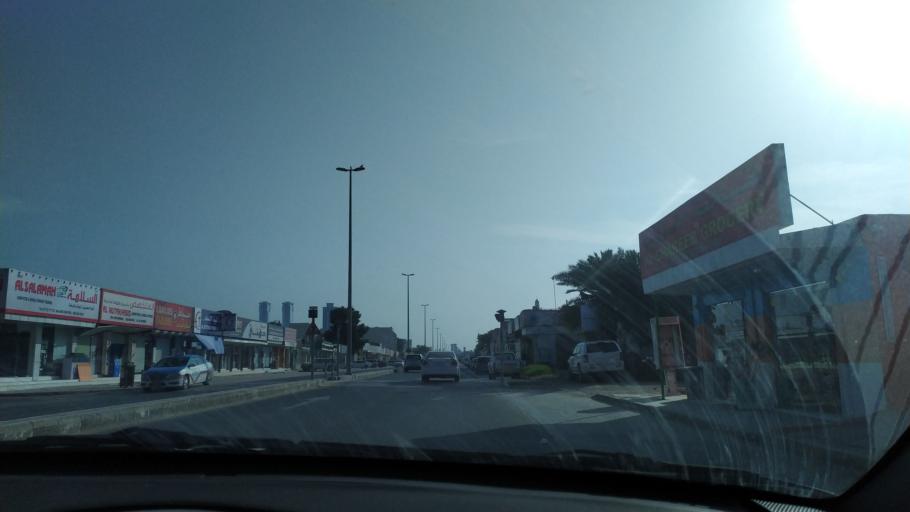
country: AE
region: Ra's al Khaymah
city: Ras al-Khaimah
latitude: 25.8102
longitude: 55.9642
